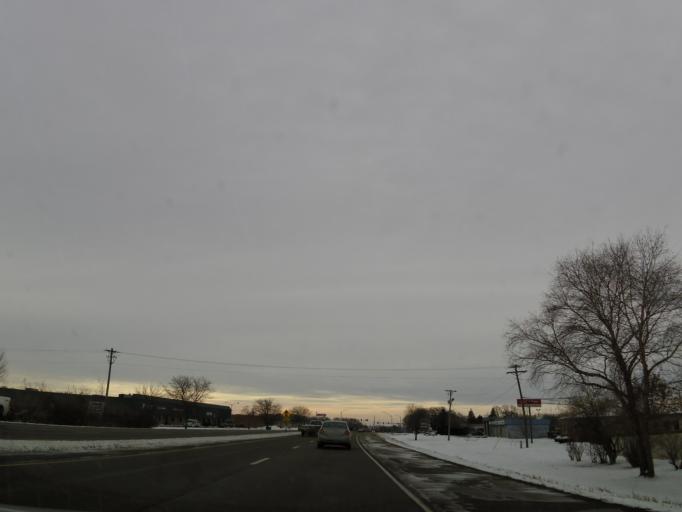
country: US
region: Illinois
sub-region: LaSalle County
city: Peru
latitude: 41.3415
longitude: -89.1205
